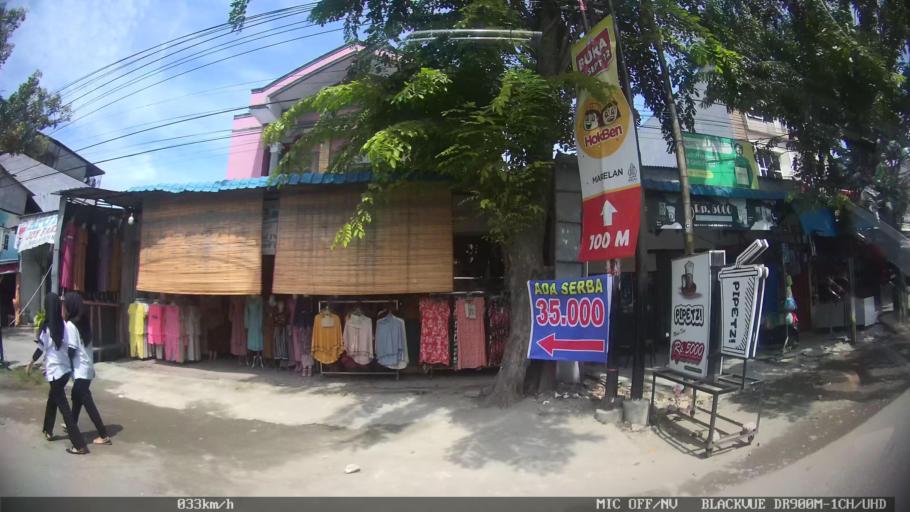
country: ID
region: North Sumatra
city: Labuhan Deli
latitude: 3.6803
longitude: 98.6561
